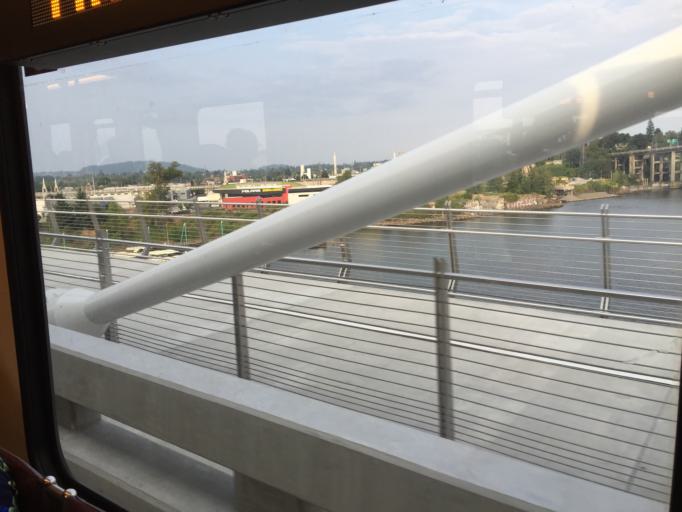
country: US
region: Oregon
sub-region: Multnomah County
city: Portland
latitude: 45.5046
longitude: -122.6675
